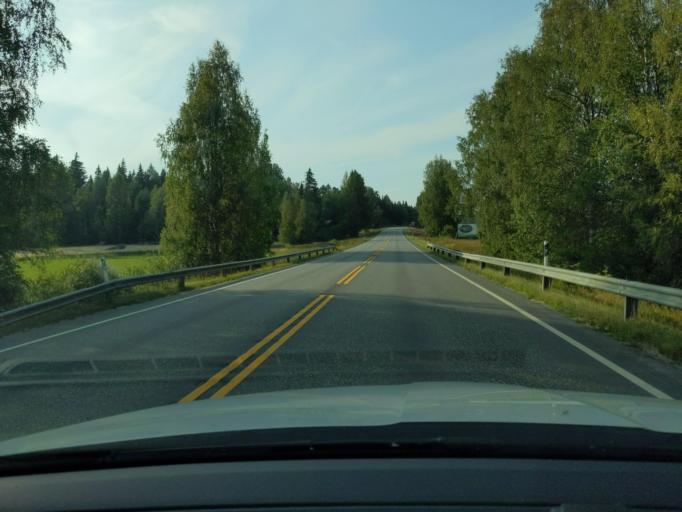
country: FI
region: Paijanne Tavastia
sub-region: Lahti
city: Padasjoki
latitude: 61.3232
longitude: 25.2784
